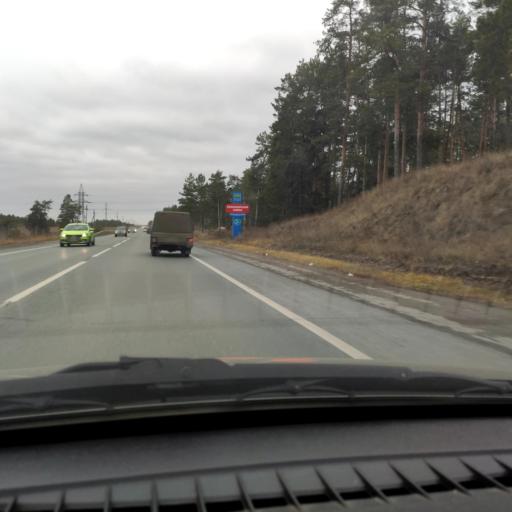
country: RU
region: Samara
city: Volzhskiy
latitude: 53.4469
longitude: 50.0987
